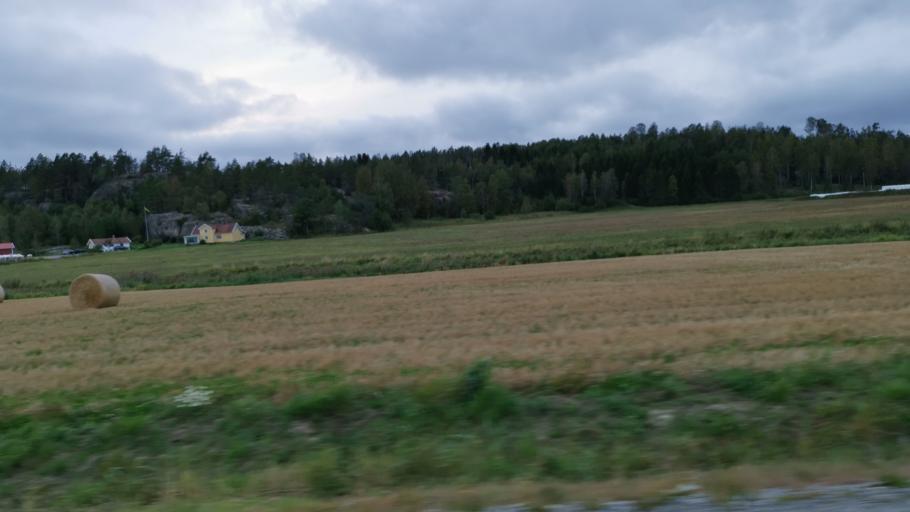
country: SE
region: Vaestra Goetaland
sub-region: Tanums Kommun
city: Tanumshede
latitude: 58.6591
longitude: 11.3463
